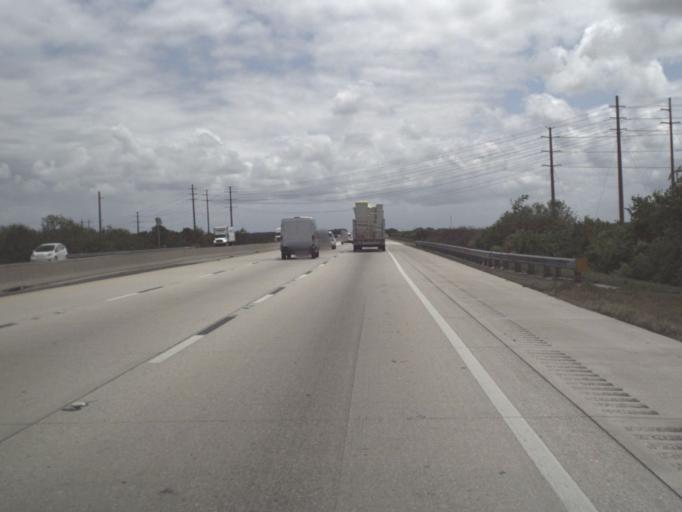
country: US
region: Florida
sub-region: Brevard County
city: Cocoa West
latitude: 28.3308
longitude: -80.7757
